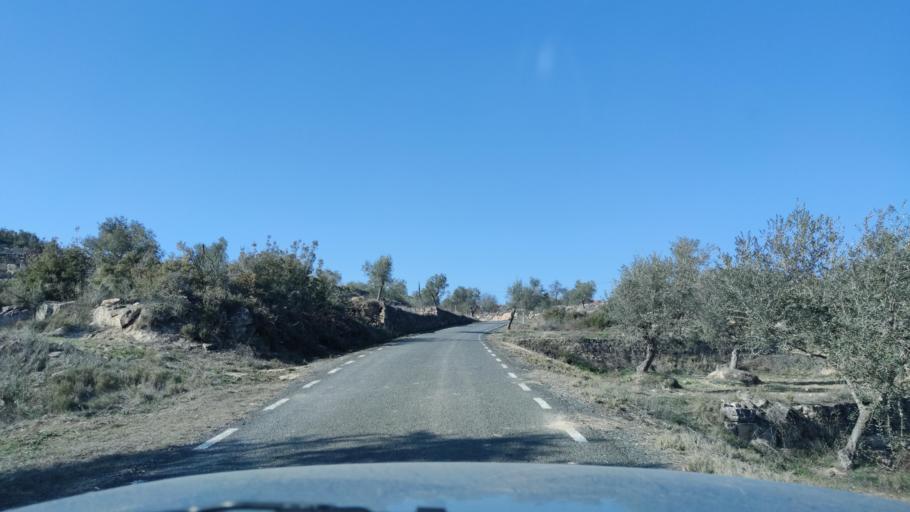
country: ES
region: Catalonia
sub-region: Provincia de Lleida
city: Torrebesses
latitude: 41.4352
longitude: 0.5700
